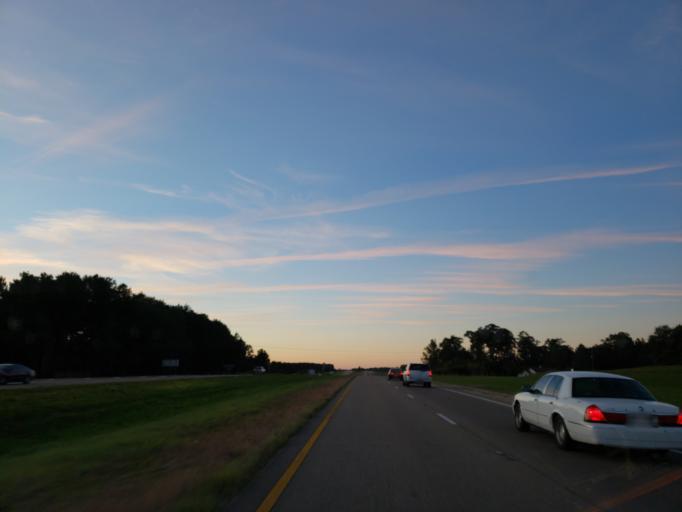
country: US
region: Mississippi
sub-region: Wayne County
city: Waynesboro
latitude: 31.7010
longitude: -88.6209
